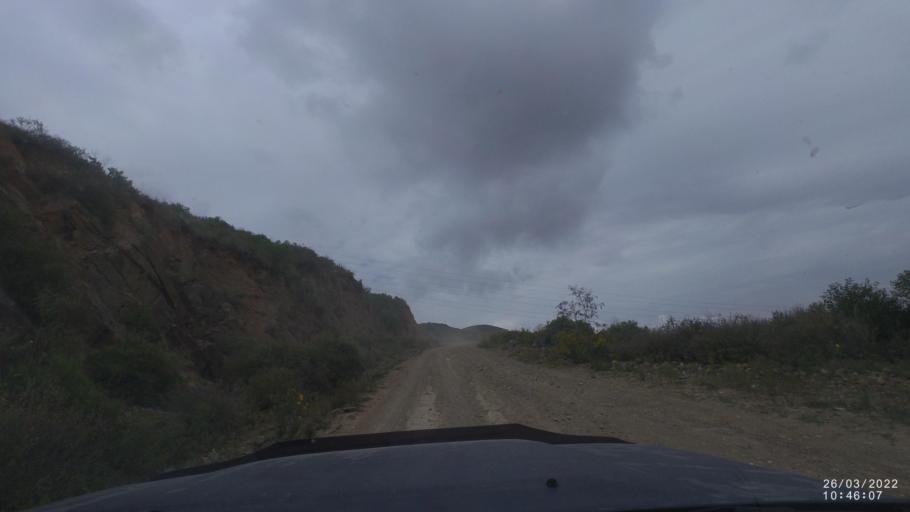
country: BO
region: Cochabamba
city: Tarata
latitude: -17.4845
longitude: -66.0492
